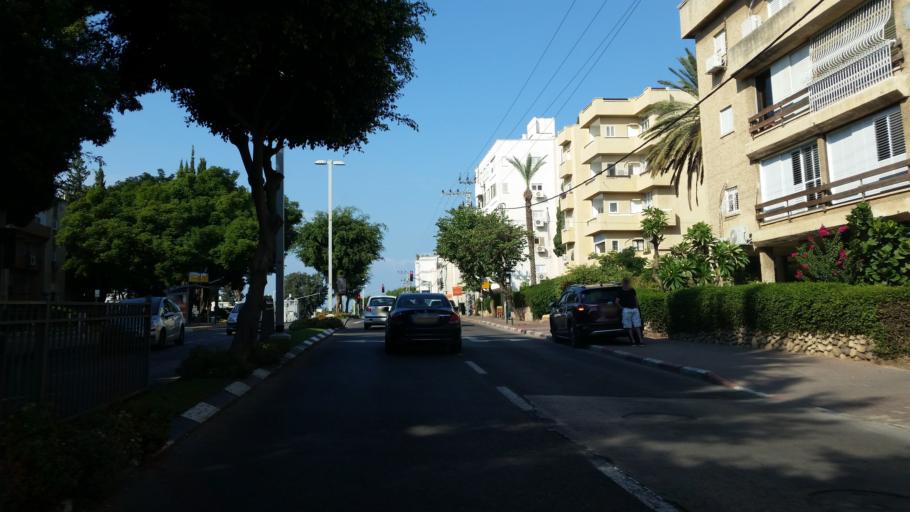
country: IL
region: Tel Aviv
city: Herzliyya
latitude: 32.1622
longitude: 34.8358
